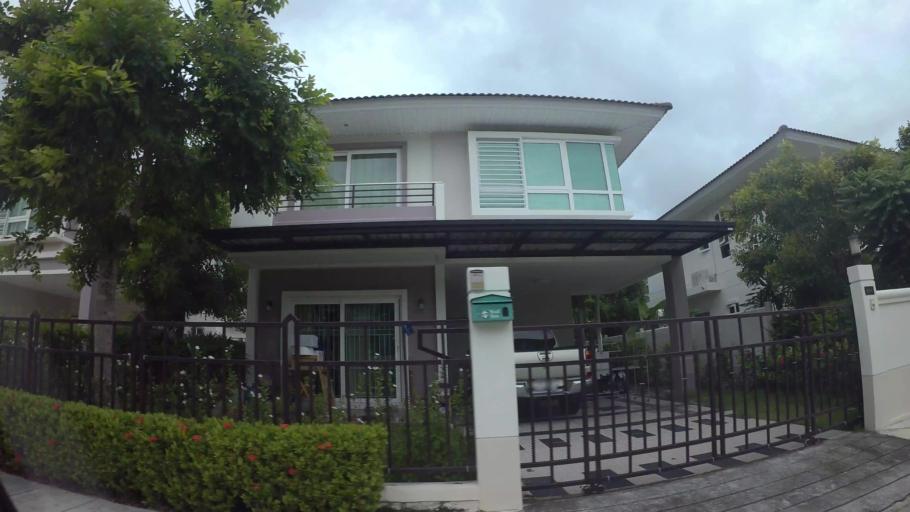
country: TH
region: Rayong
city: Rayong
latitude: 12.6815
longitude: 101.2812
